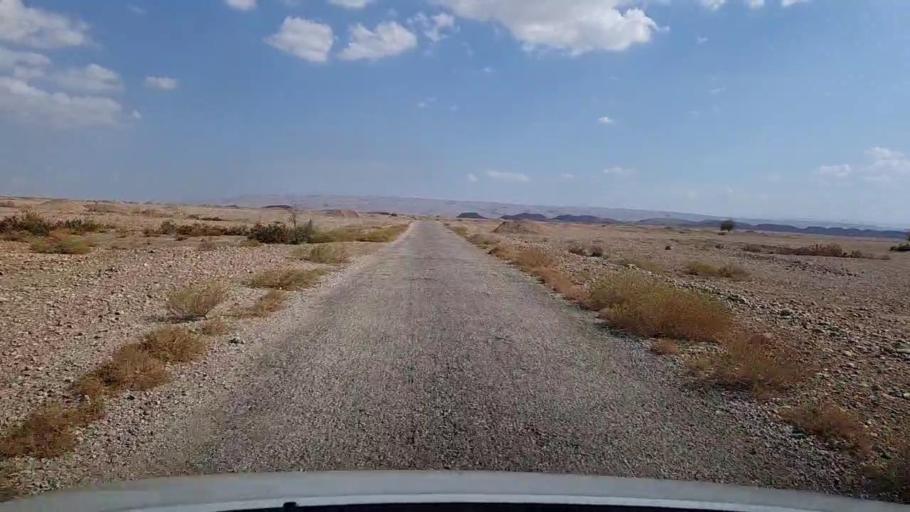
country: PK
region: Sindh
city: Bhan
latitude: 26.3659
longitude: 67.6403
